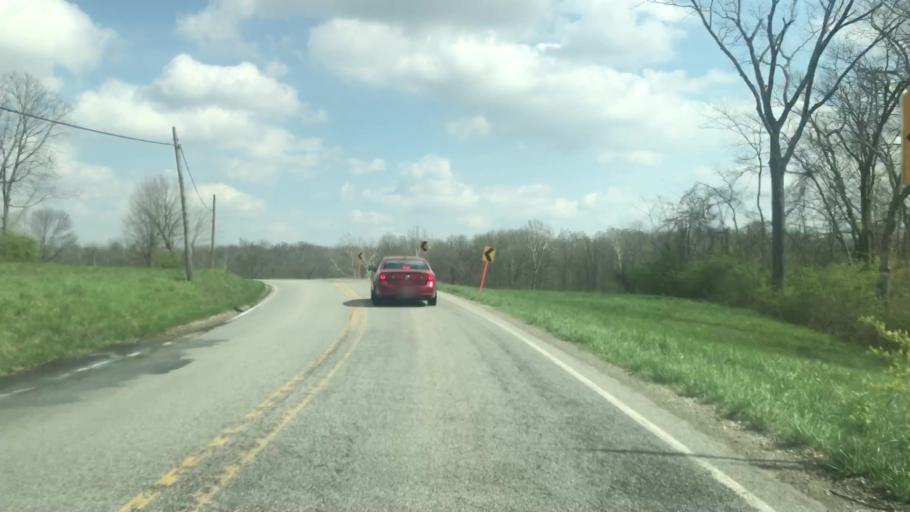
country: US
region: Indiana
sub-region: Johnson County
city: Waterloo
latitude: 39.5532
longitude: -86.2166
